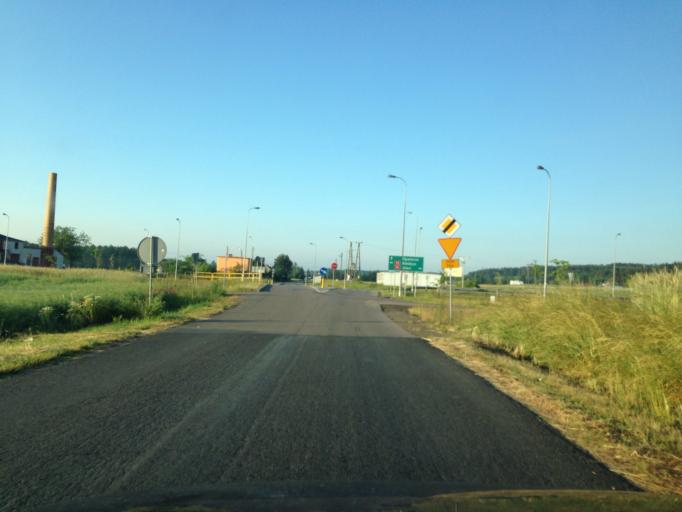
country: PL
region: Pomeranian Voivodeship
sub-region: Powiat tczewski
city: Gniew
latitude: 53.7607
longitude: 18.8216
